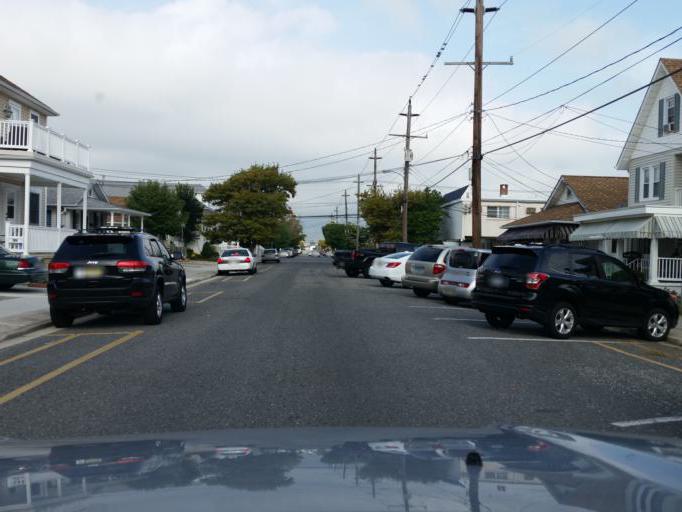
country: US
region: New Jersey
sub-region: Cape May County
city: Wildwood Crest
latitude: 38.9815
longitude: -74.8266
